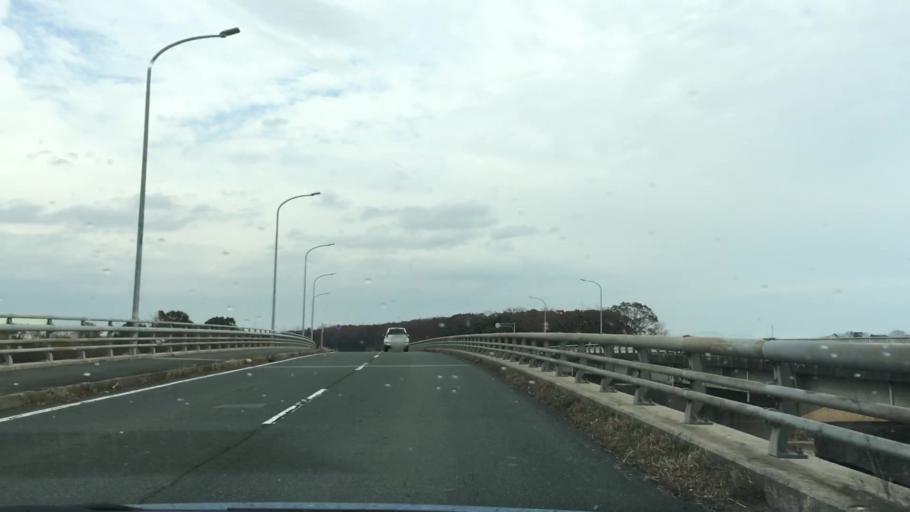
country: JP
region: Aichi
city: Tahara
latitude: 34.6935
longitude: 137.3223
